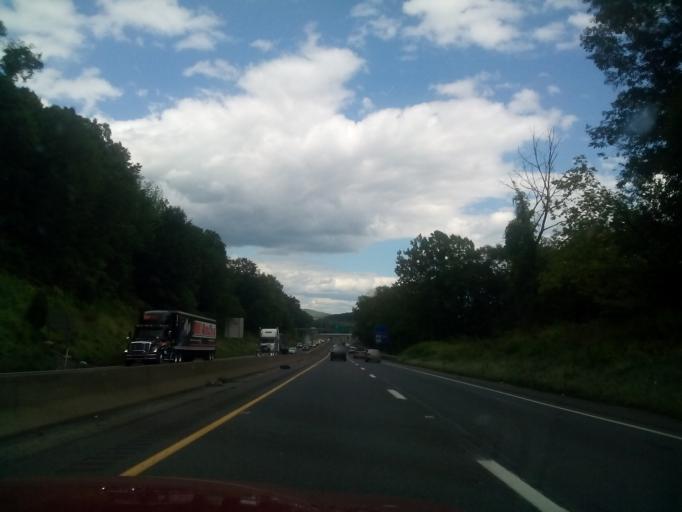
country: US
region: Pennsylvania
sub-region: Monroe County
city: East Stroudsburg
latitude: 40.9955
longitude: -75.1634
